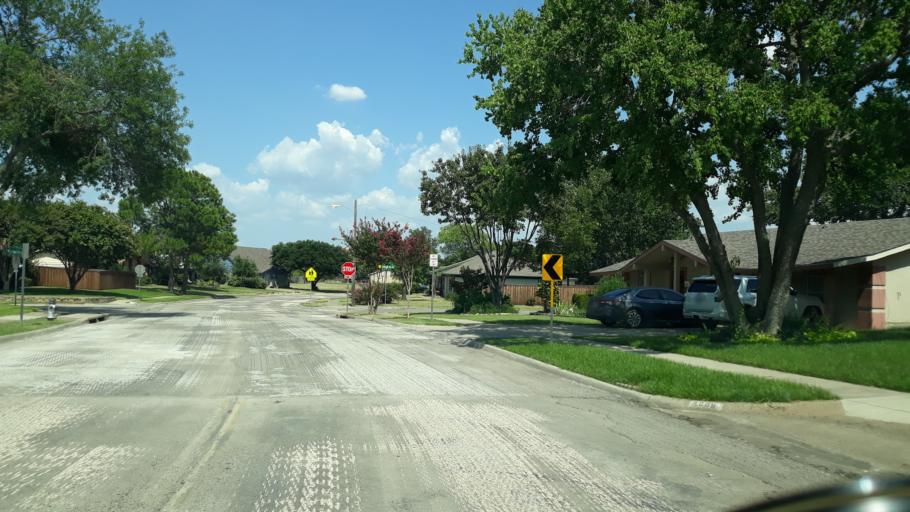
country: US
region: Texas
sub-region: Dallas County
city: Irving
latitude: 32.8509
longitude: -97.0047
